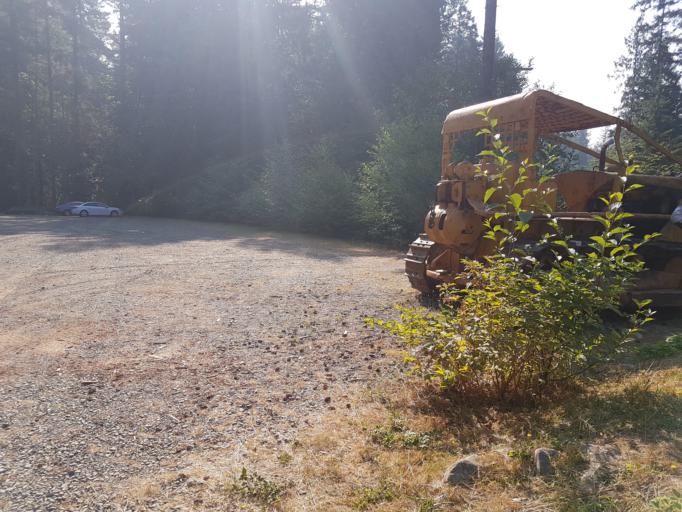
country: CA
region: British Columbia
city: Port Alberni
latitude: 49.3087
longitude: -124.8289
